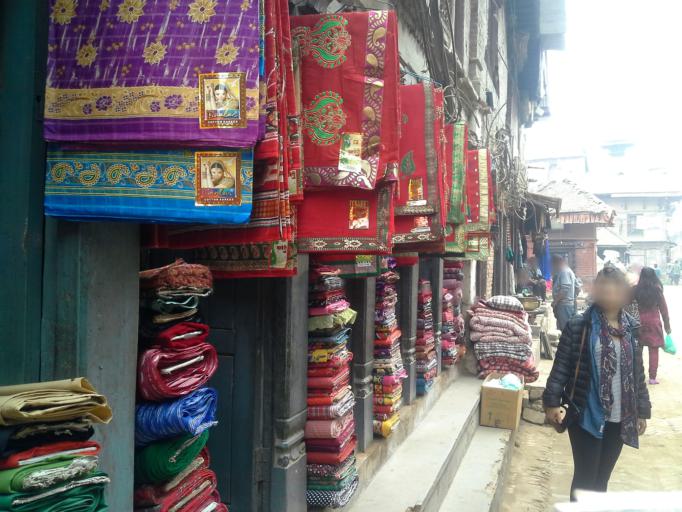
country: NP
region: Central Region
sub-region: Bagmati Zone
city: Bhaktapur
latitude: 27.6726
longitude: 85.4321
